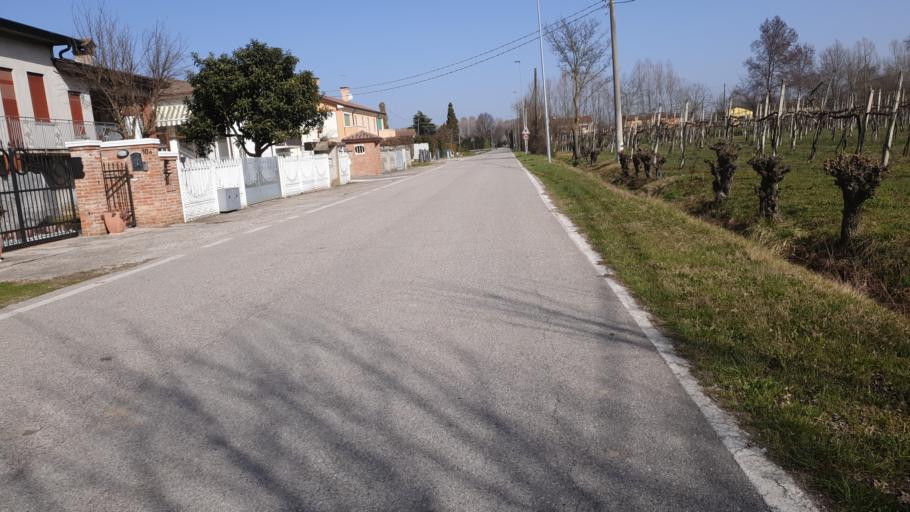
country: IT
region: Veneto
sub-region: Provincia di Padova
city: Cavino
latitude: 45.5174
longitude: 11.8990
